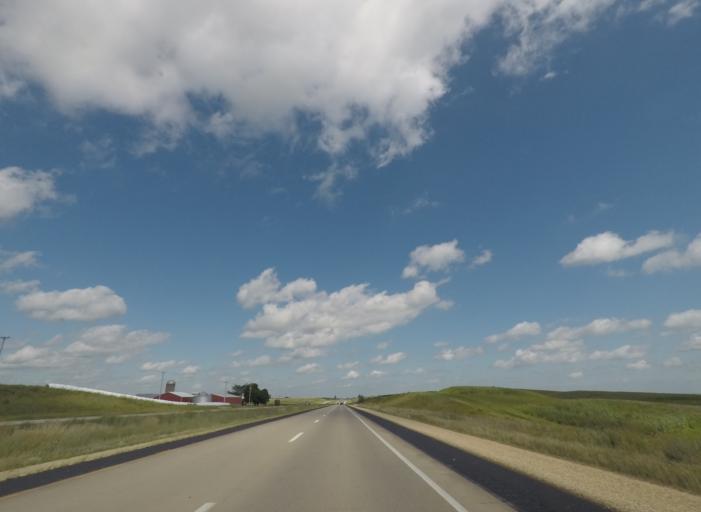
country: US
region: Iowa
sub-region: Dubuque County
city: Cascade
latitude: 42.2915
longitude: -91.0656
